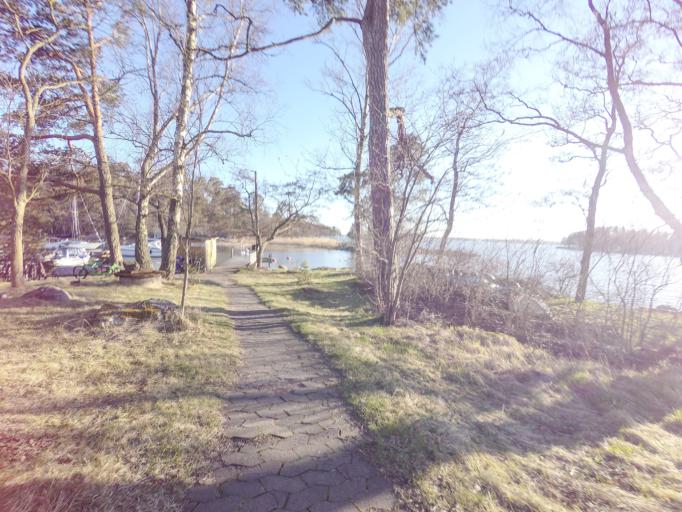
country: FI
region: Uusimaa
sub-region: Helsinki
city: Helsinki
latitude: 60.1797
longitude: 25.0230
